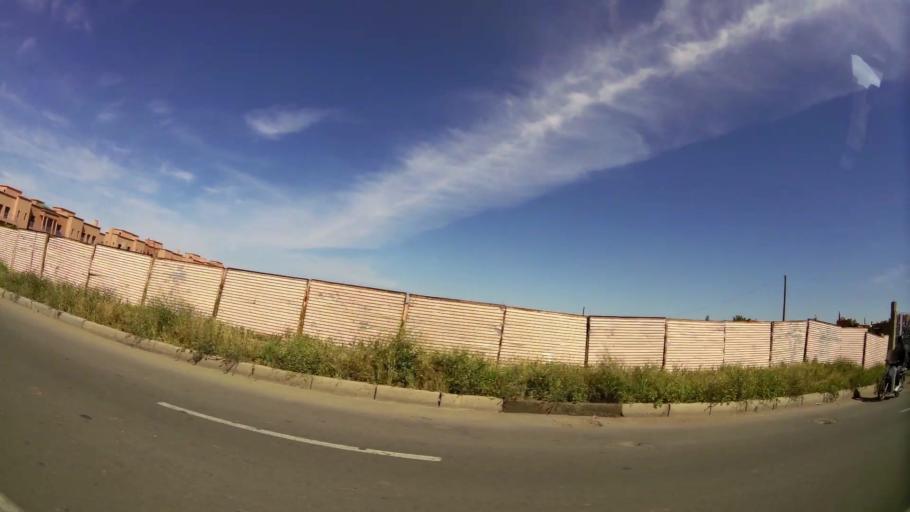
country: MA
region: Marrakech-Tensift-Al Haouz
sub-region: Marrakech
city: Marrakesh
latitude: 31.6539
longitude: -8.0600
